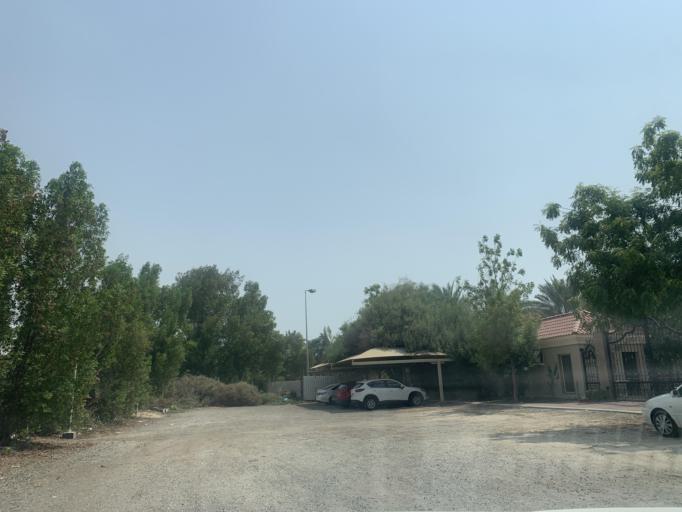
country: BH
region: Central Governorate
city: Madinat Hamad
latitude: 26.1601
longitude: 50.4540
